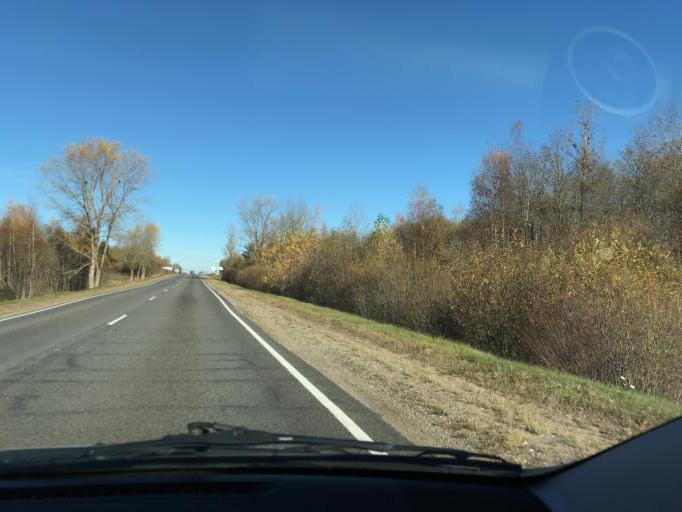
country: BY
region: Vitebsk
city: Lyepyel'
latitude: 55.0357
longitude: 28.7481
